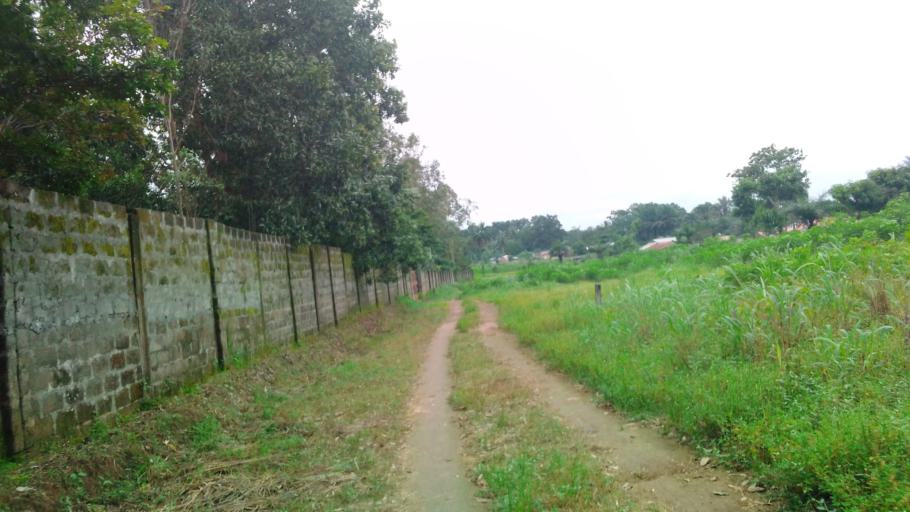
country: SL
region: Northern Province
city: Lunsar
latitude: 8.6964
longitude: -12.5487
